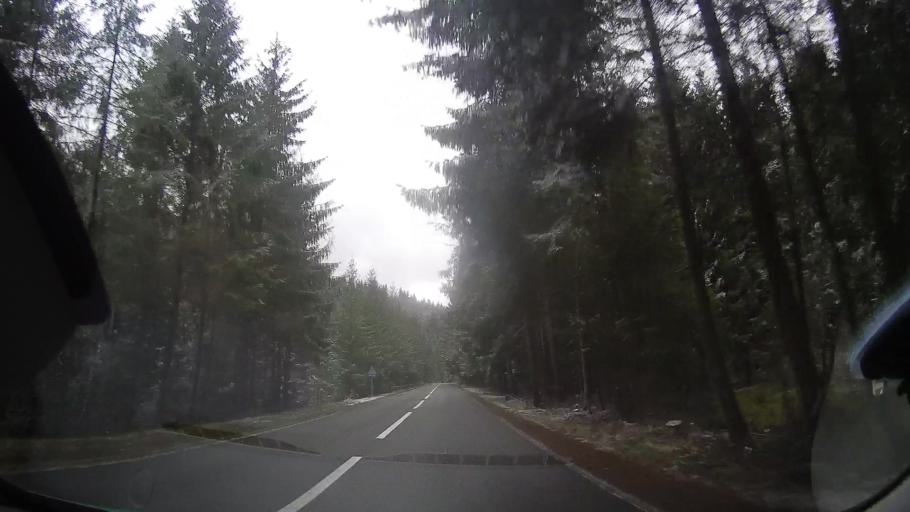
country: RO
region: Cluj
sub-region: Comuna Calatele
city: Calatele
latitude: 46.7389
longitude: 23.0186
